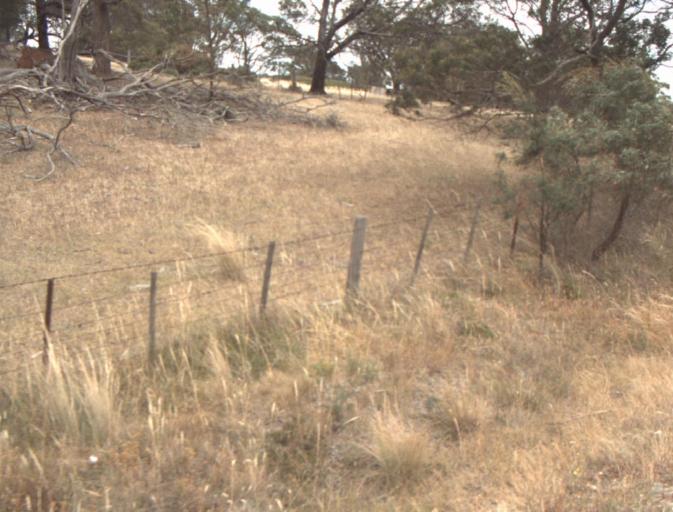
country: AU
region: Tasmania
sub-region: Northern Midlands
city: Evandale
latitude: -41.5127
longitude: 147.3049
